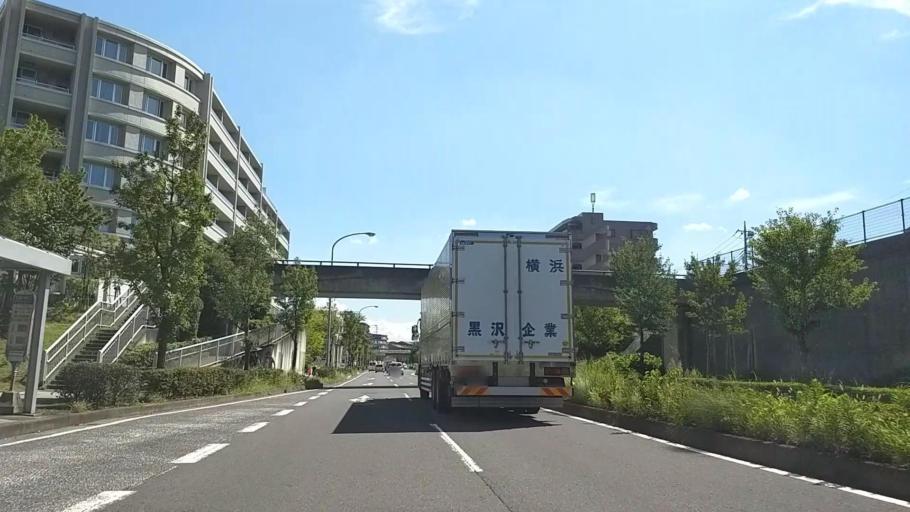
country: JP
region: Tokyo
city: Chofugaoka
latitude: 35.5639
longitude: 139.5818
